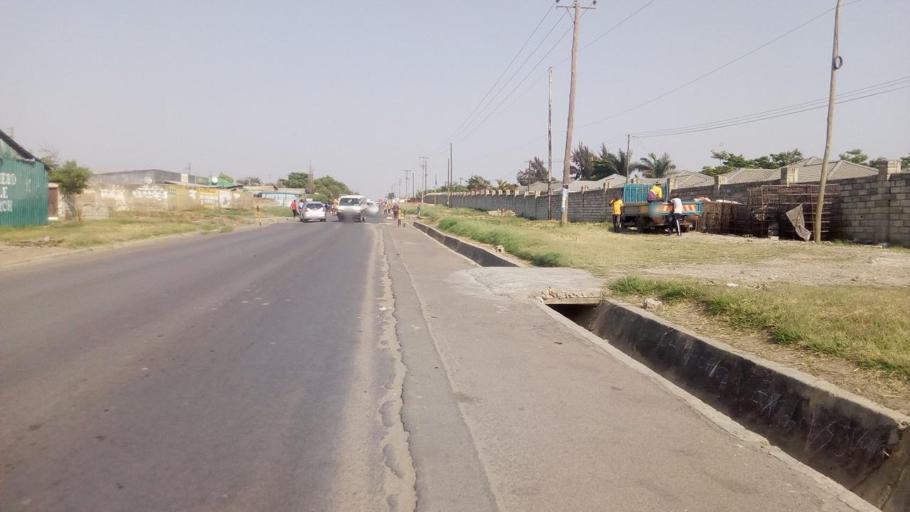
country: ZM
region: Lusaka
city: Lusaka
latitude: -15.3688
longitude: 28.2857
